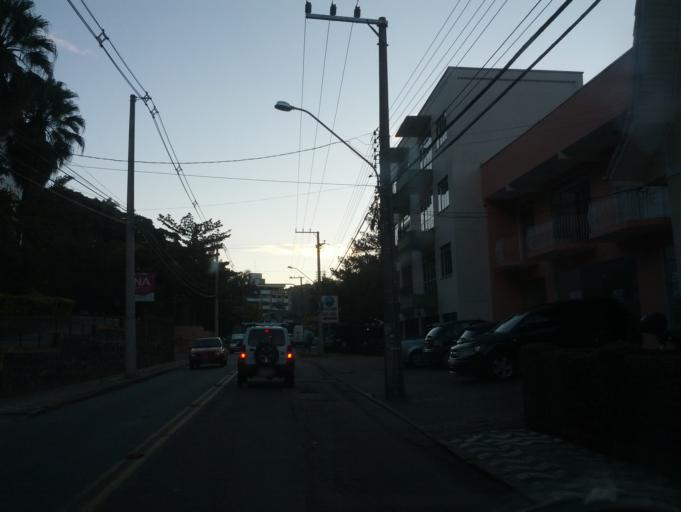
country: BR
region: Santa Catarina
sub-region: Blumenau
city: Blumenau
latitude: -26.9254
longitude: -49.0709
